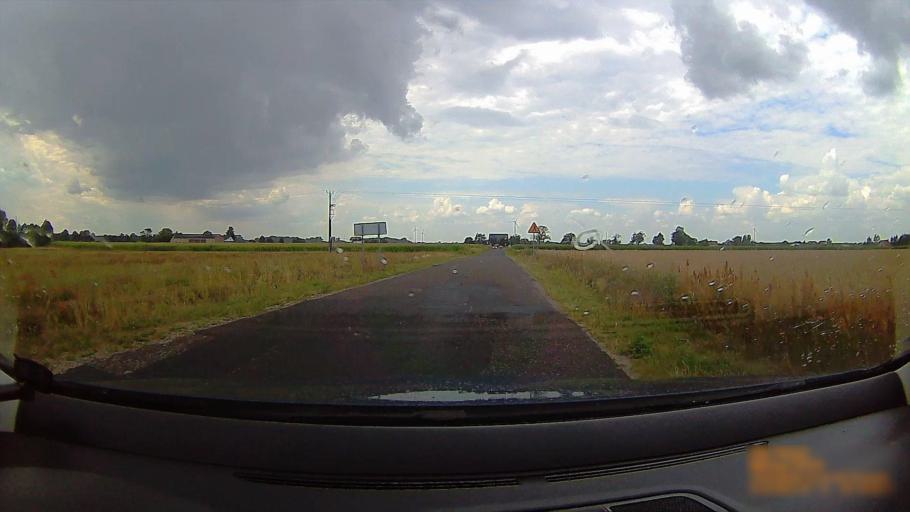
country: PL
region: Greater Poland Voivodeship
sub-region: Powiat koninski
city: Rychwal
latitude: 52.1027
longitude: 18.1714
